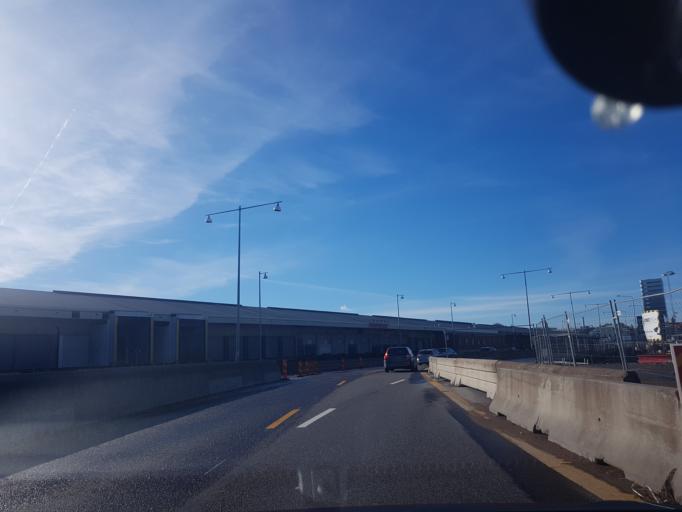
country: SE
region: Vaestra Goetaland
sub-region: Goteborg
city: Goeteborg
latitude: 57.7153
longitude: 11.9802
